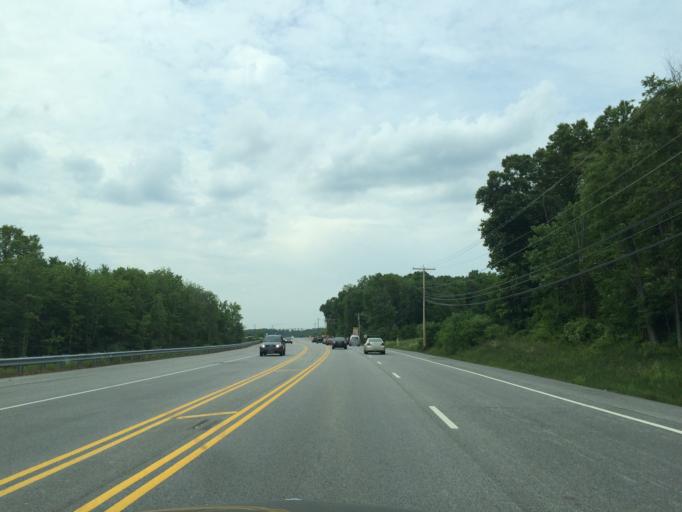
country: US
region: Maryland
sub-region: Carroll County
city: Sykesville
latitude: 39.3126
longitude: -76.8985
